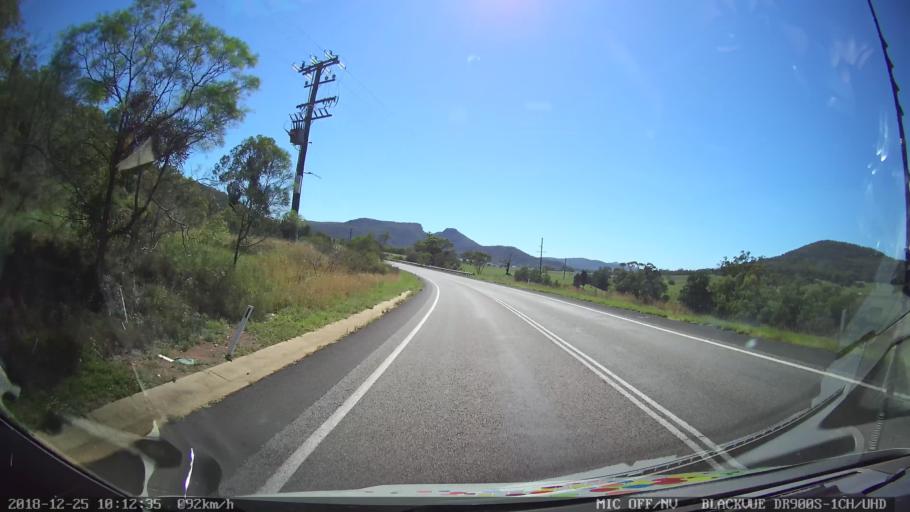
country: AU
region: New South Wales
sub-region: Muswellbrook
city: Denman
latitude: -32.3290
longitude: 150.5328
